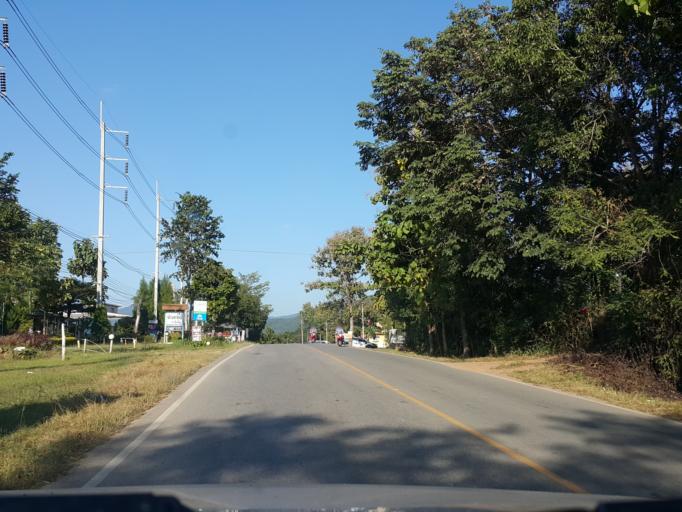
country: TH
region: Mae Hong Son
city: Mae Hi
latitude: 19.3376
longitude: 98.4322
